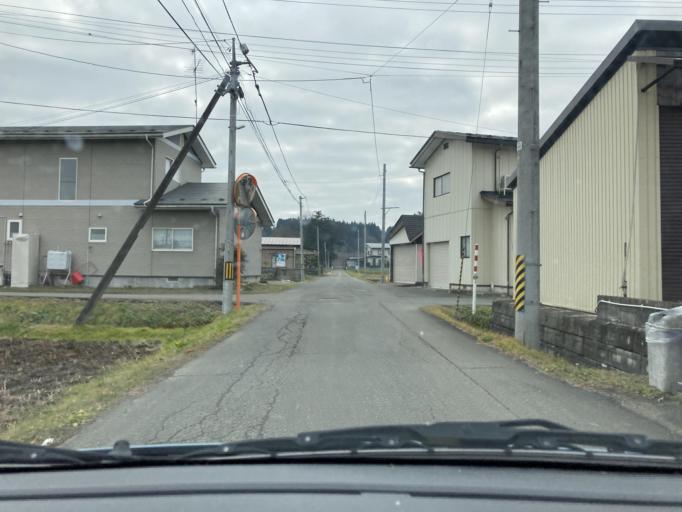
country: JP
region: Iwate
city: Kitakami
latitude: 39.2787
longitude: 141.0766
